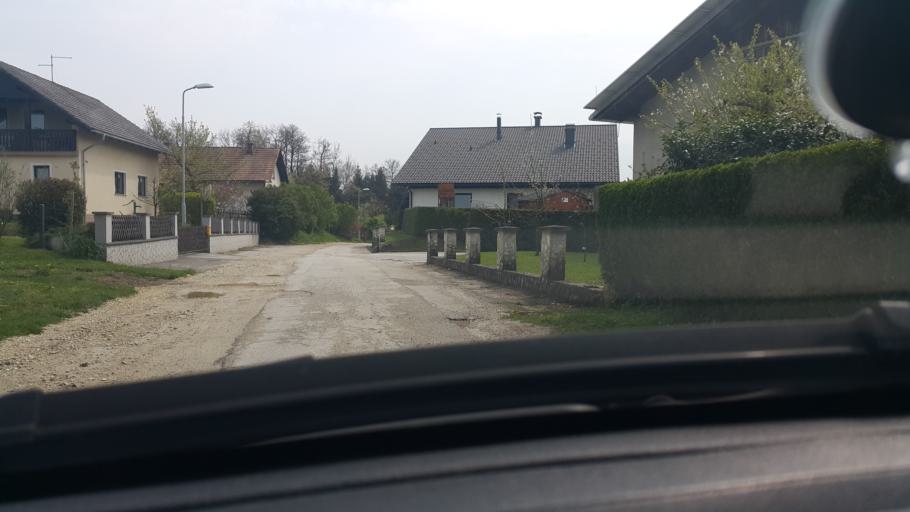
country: SI
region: Brezice
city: Brezice
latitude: 45.9071
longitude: 15.6506
